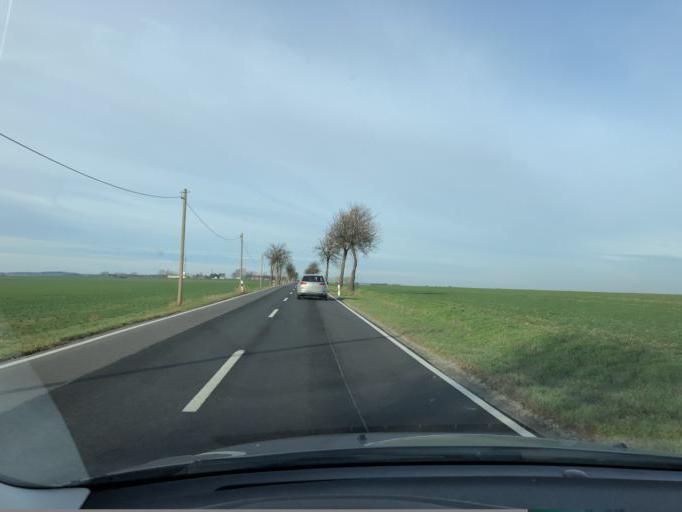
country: DE
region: Saxony-Anhalt
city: Uichteritz
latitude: 51.2348
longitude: 11.9029
